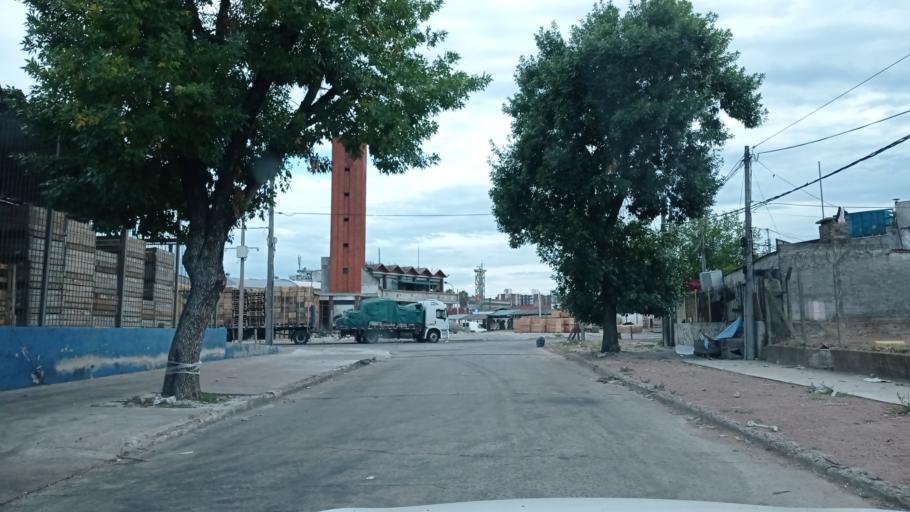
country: UY
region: Montevideo
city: Montevideo
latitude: -34.8708
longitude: -56.1558
